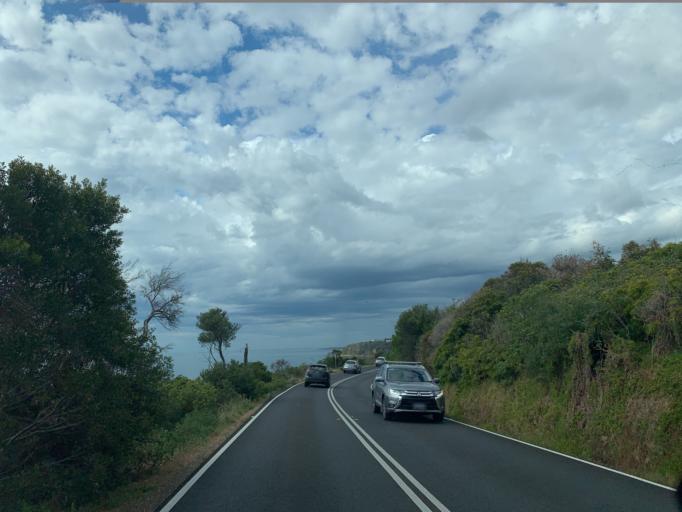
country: AU
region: Victoria
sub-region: Mornington Peninsula
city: Mount Martha
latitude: -38.2844
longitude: 144.9934
